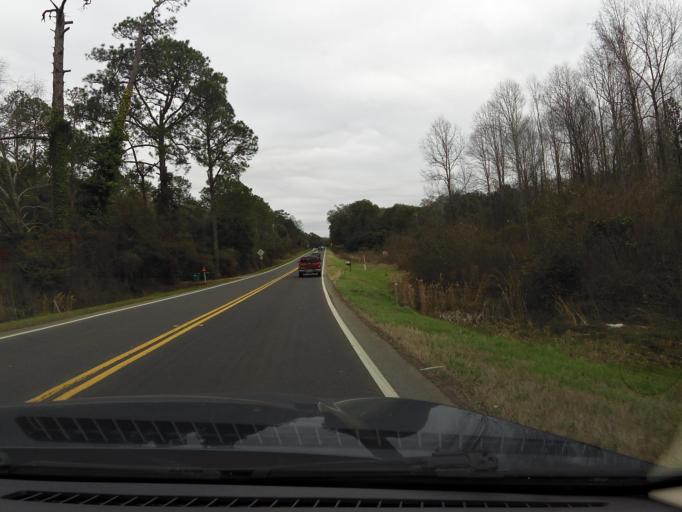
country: US
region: Georgia
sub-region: Randolph County
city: Shellman
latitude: 31.7821
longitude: -84.6009
